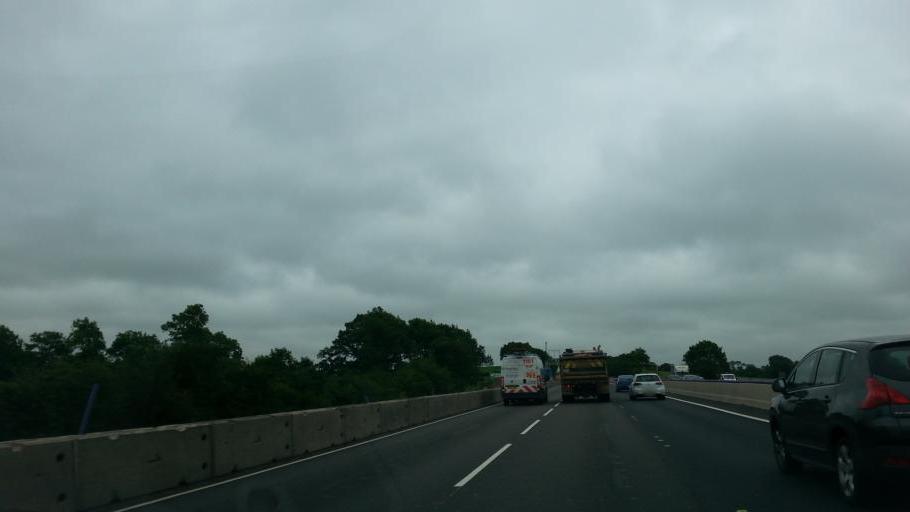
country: GB
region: England
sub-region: Northamptonshire
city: Long Buckby
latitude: 52.3442
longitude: -1.1527
